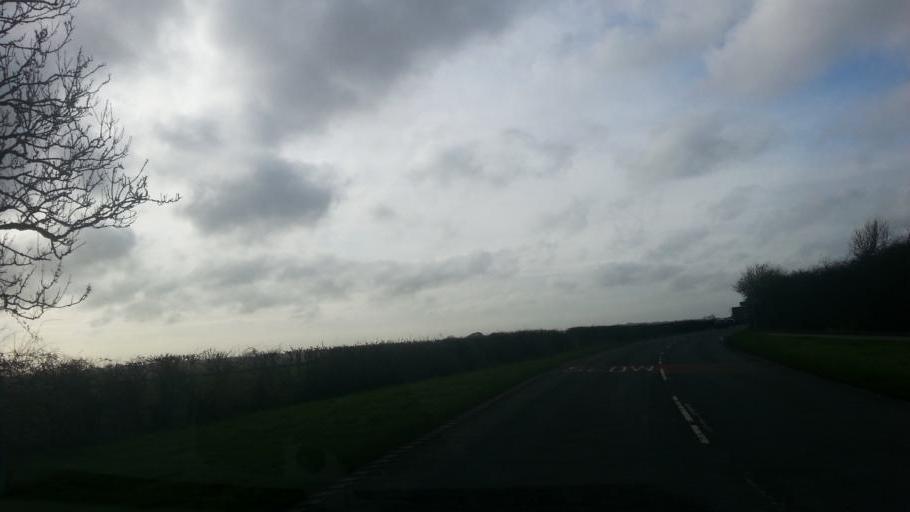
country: GB
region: England
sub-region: District of Rutland
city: Wing
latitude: 52.6347
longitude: -0.6758
